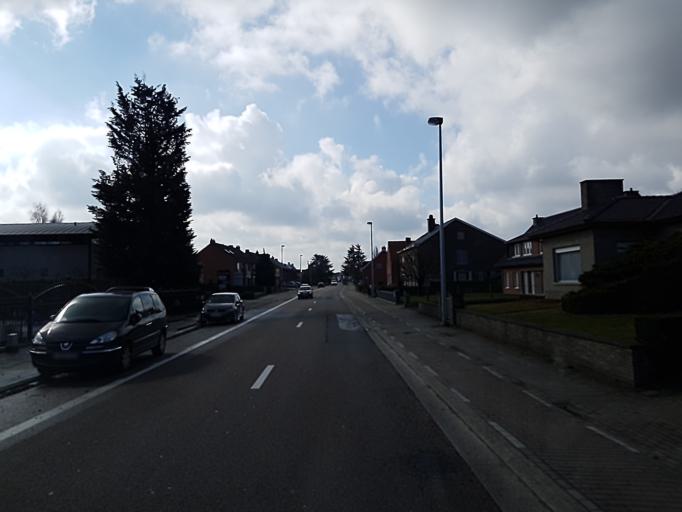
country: BE
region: Flanders
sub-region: Provincie Oost-Vlaanderen
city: Sint-Niklaas
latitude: 51.1722
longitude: 4.1127
